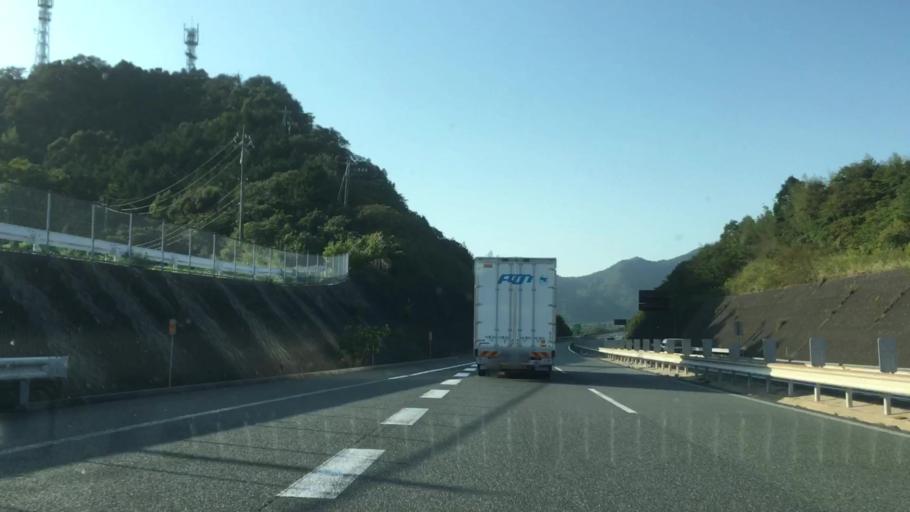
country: JP
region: Yamaguchi
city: Ogori-shimogo
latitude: 34.0893
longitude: 131.4605
